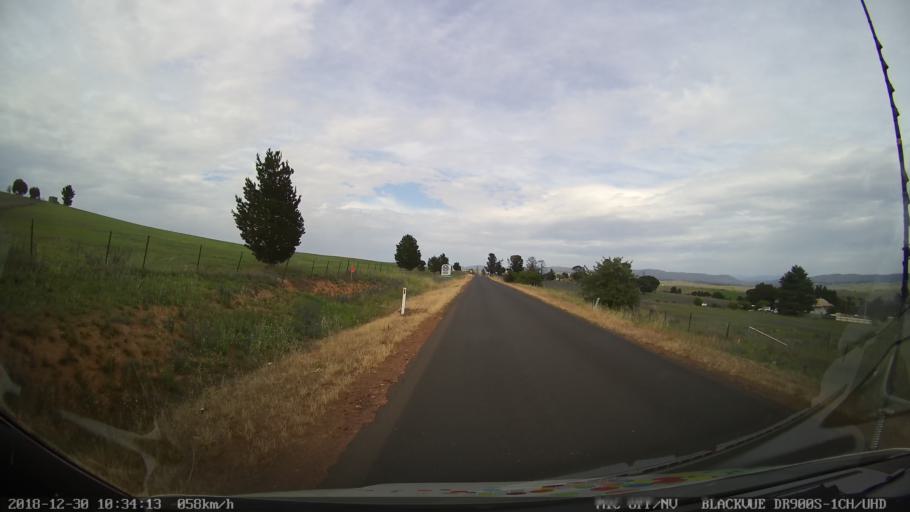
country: AU
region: New South Wales
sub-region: Snowy River
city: Berridale
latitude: -36.5001
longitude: 148.8429
